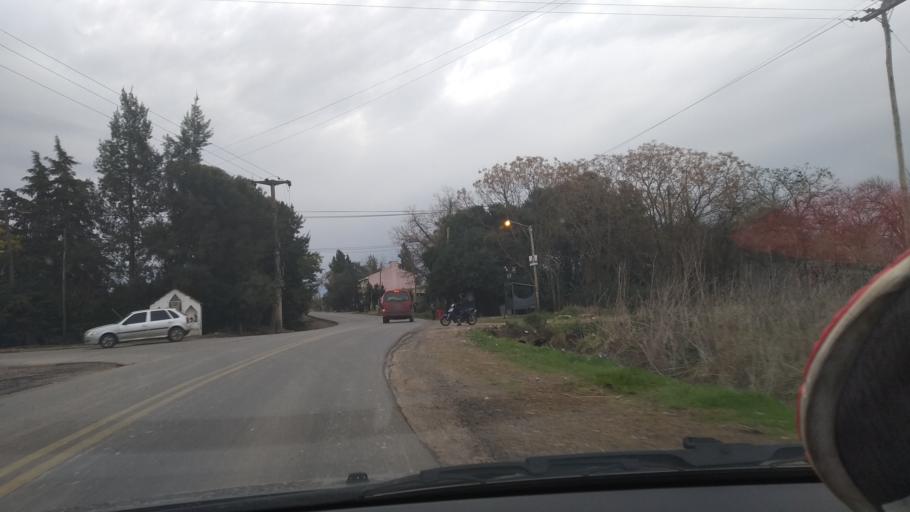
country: AR
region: Buenos Aires
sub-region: Partido de La Plata
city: La Plata
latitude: -34.9959
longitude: -58.0732
